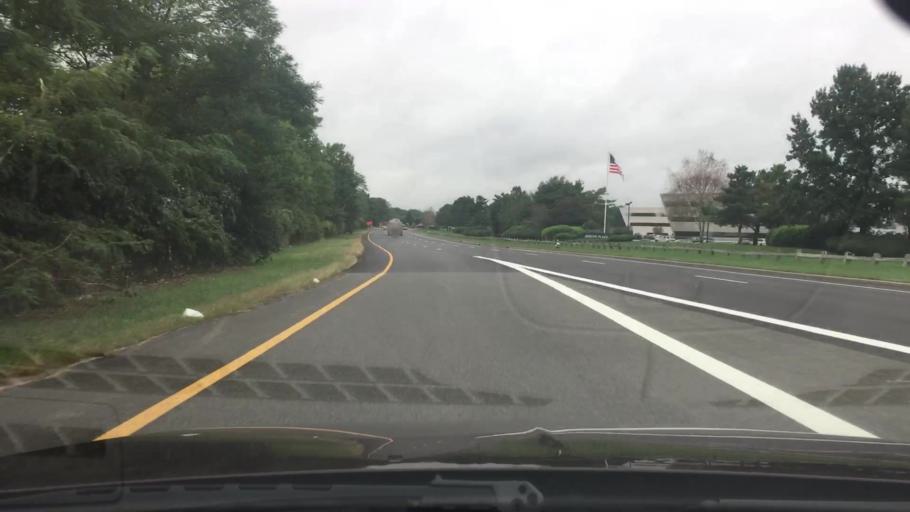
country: US
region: New York
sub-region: Nassau County
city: Jericho
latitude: 40.7839
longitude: -73.5460
